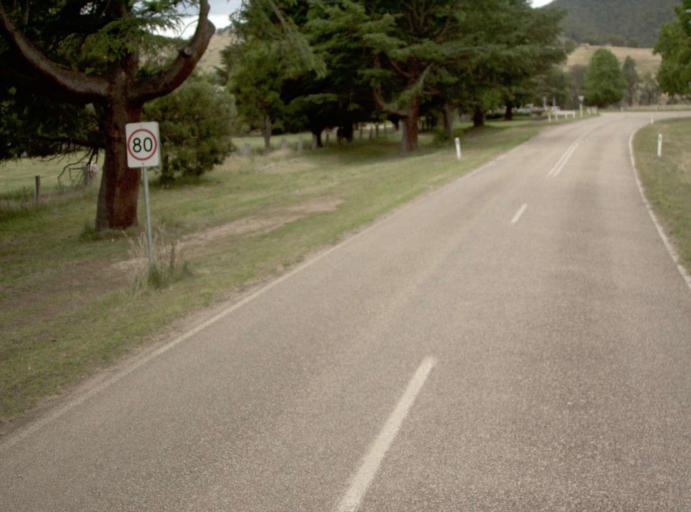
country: AU
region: Victoria
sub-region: East Gippsland
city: Bairnsdale
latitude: -37.4688
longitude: 147.2543
